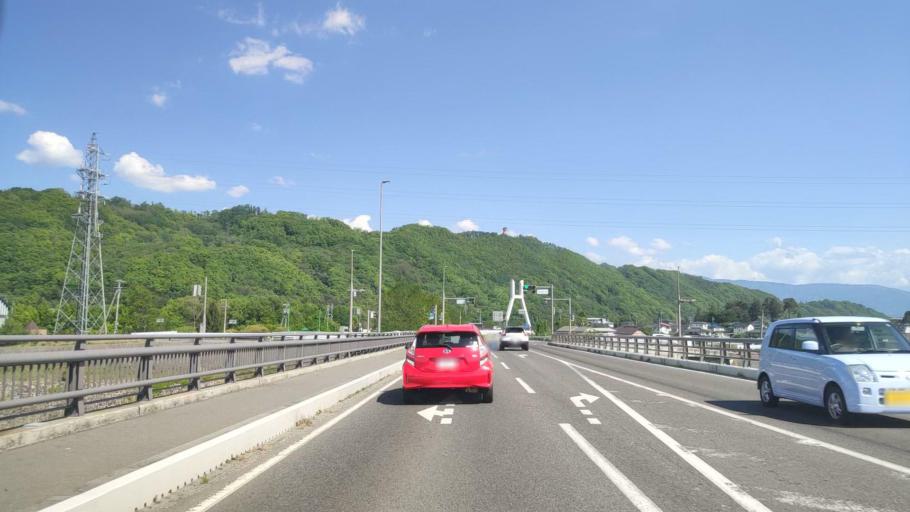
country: JP
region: Nagano
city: Matsumoto
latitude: 36.2690
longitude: 137.9384
